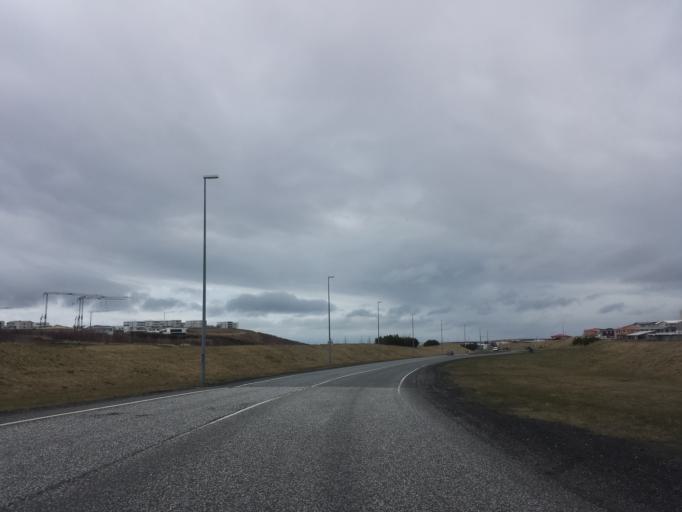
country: IS
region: Capital Region
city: Reykjavik
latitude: 64.0890
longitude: -21.8378
